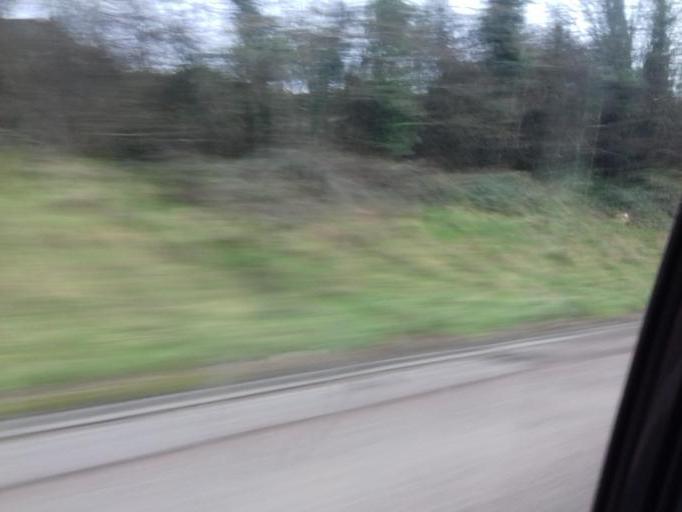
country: GB
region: Northern Ireland
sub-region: Lisburn District
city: Lisburn
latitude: 54.5517
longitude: -5.9966
